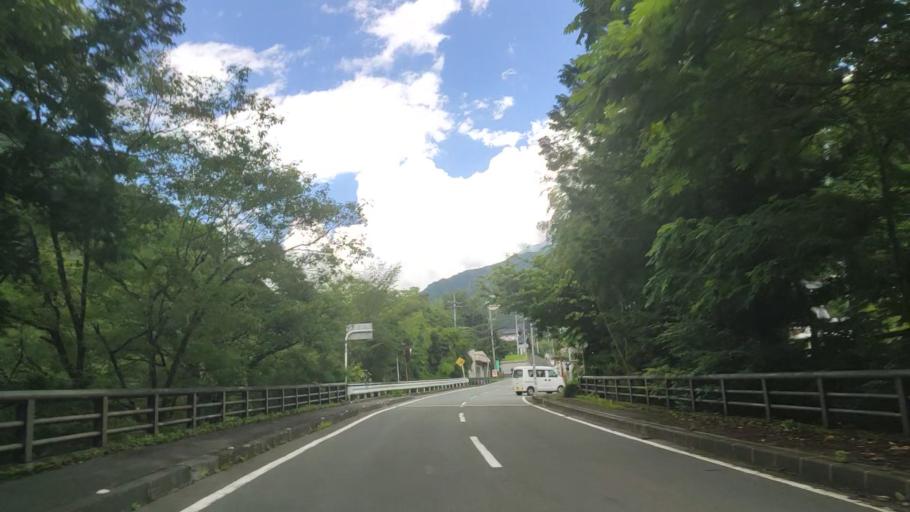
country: JP
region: Yamanashi
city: Enzan
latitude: 35.7957
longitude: 138.7405
